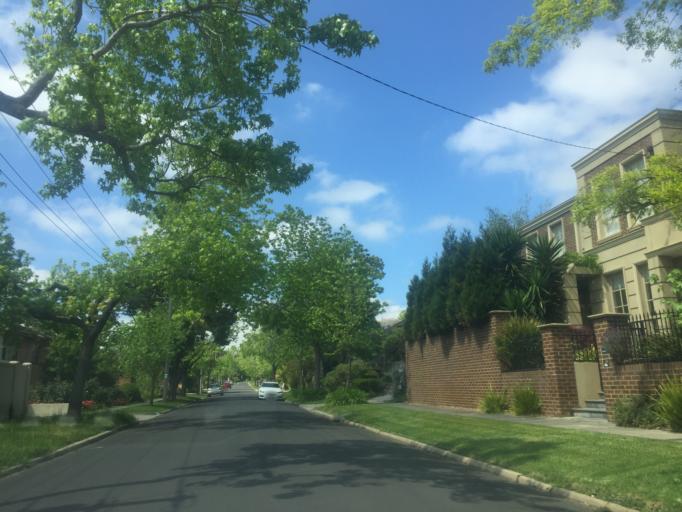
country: AU
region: Victoria
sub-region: Boroondara
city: Balwyn North
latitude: -37.8024
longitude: 145.0889
